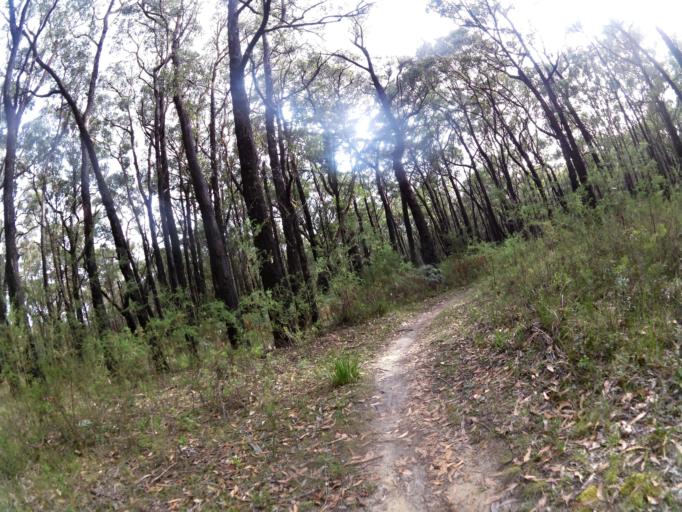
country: AU
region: Victoria
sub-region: Colac-Otway
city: Colac
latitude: -38.4981
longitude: 143.7124
